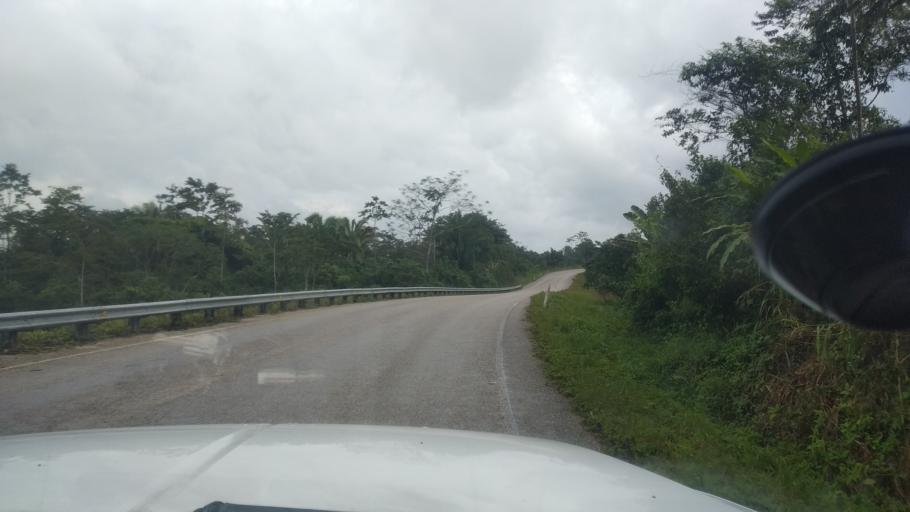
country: GT
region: Peten
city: San Luis
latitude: 16.1983
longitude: -89.1580
